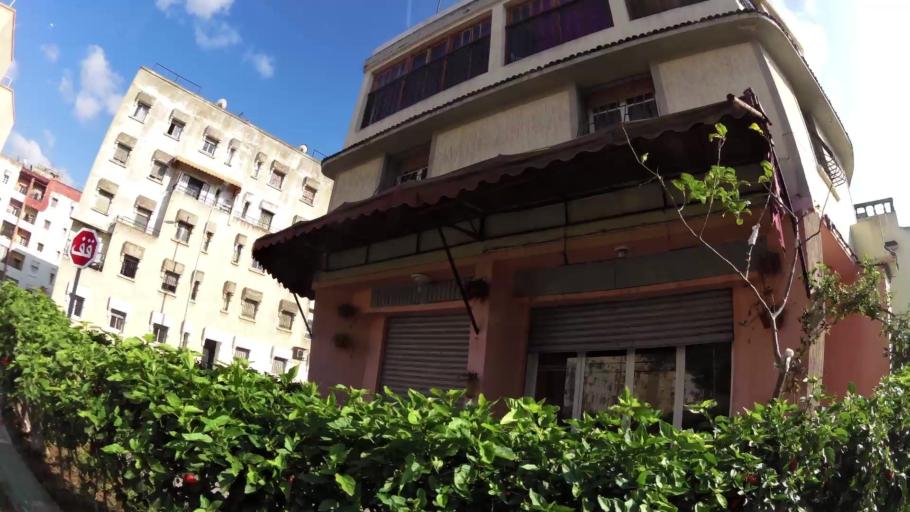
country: MA
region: Rabat-Sale-Zemmour-Zaer
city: Sale
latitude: 34.0484
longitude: -6.8076
